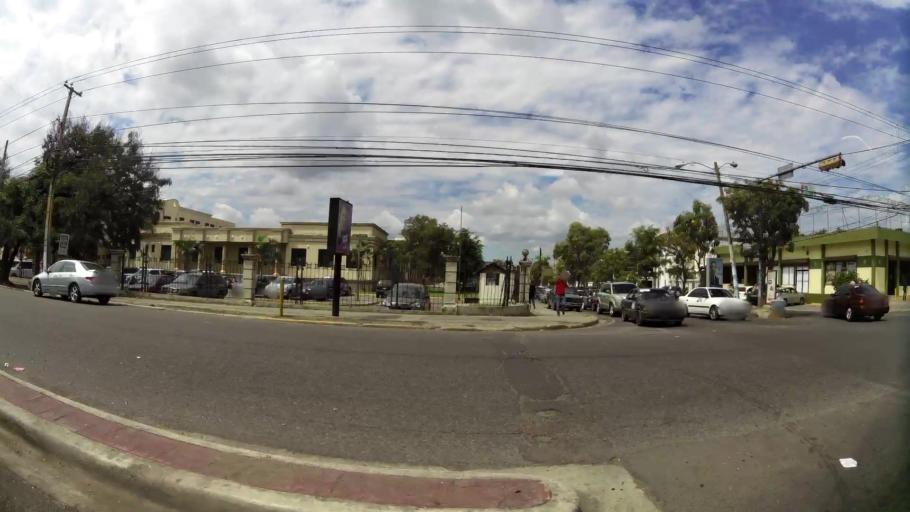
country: DO
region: Santiago
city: Santiago de los Caballeros
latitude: 19.4681
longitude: -70.7124
